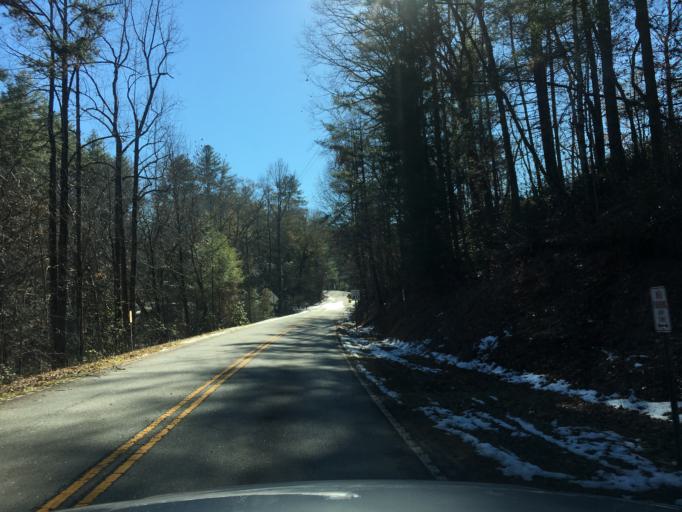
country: US
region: South Carolina
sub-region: Greenville County
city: Slater-Marietta
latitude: 35.0672
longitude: -82.6183
